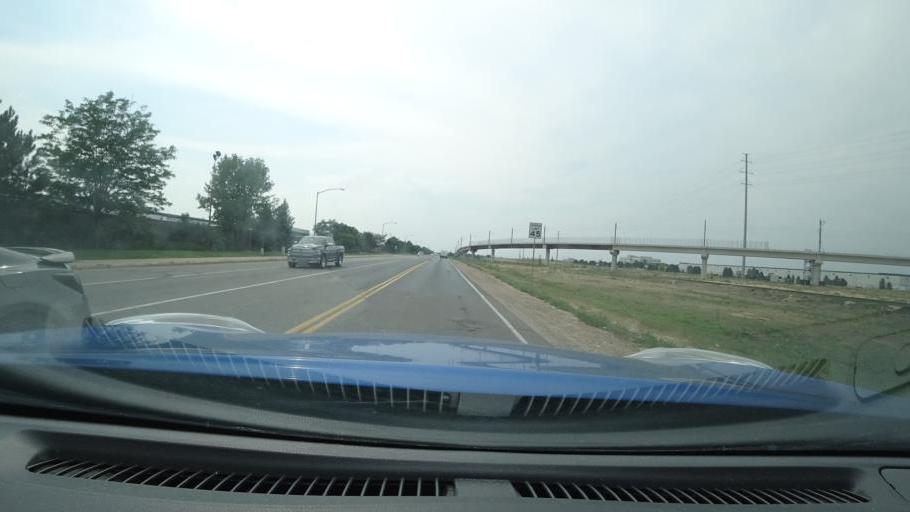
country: US
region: Colorado
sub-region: Adams County
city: Aurora
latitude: 39.7557
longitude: -104.7917
